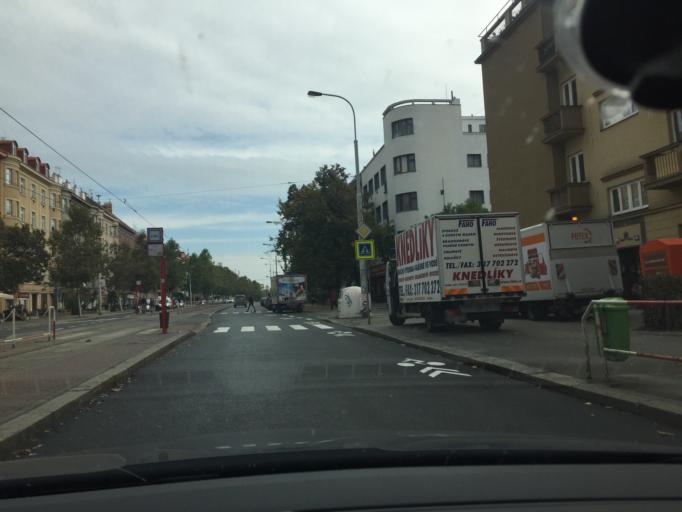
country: CZ
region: Praha
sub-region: Praha 8
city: Liben
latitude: 50.0921
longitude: 14.4805
